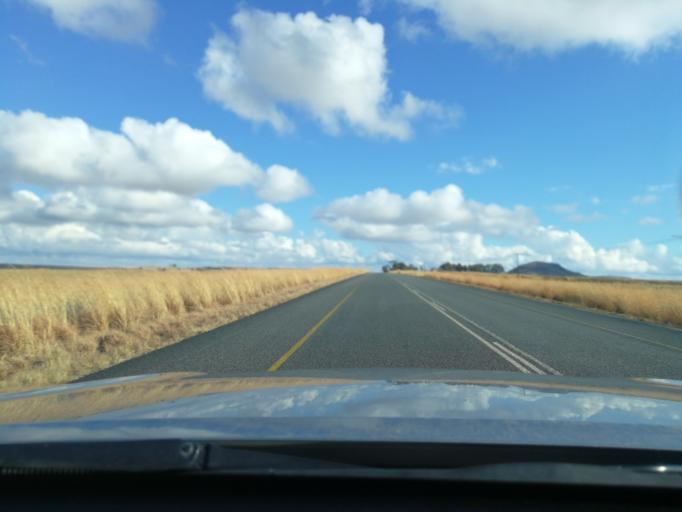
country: ZA
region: Orange Free State
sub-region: Thabo Mofutsanyana District Municipality
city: Reitz
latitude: -27.9643
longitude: 28.3793
